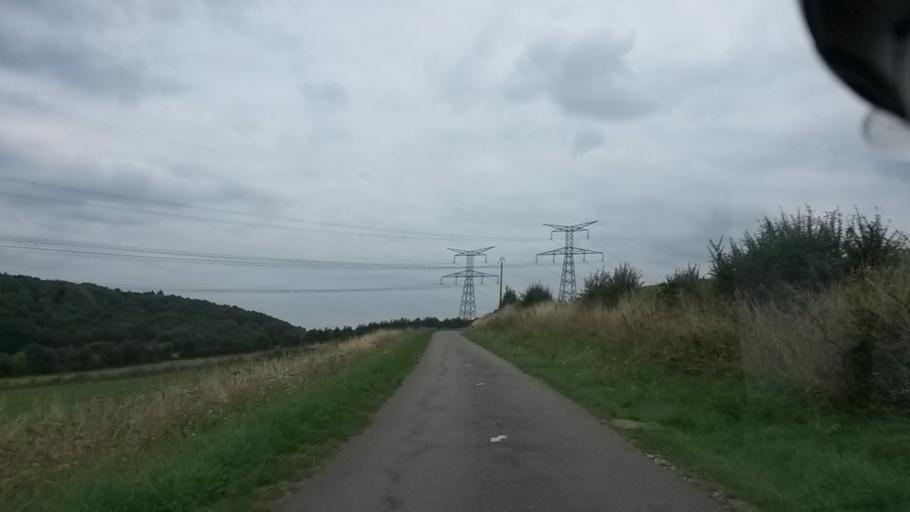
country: FR
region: Haute-Normandie
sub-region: Departement de la Seine-Maritime
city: La Feuillie
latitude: 49.4781
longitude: 1.5242
